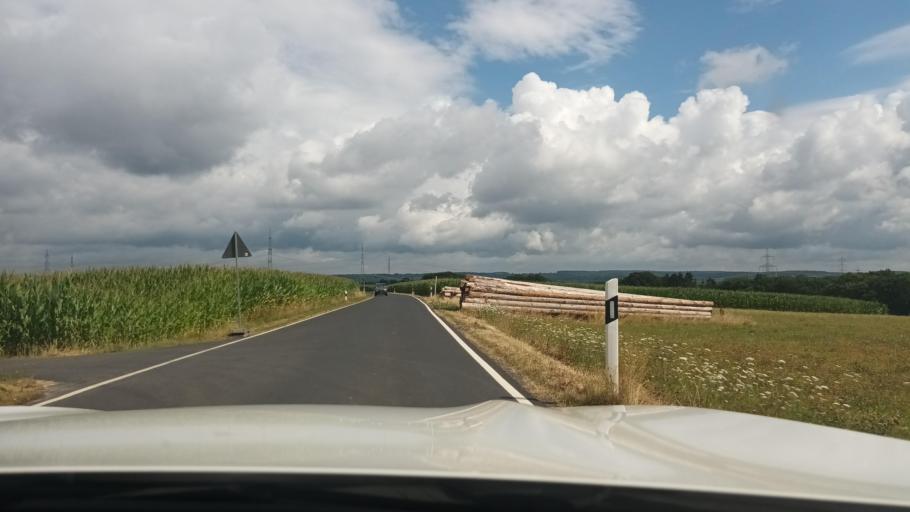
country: DE
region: North Rhine-Westphalia
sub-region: Regierungsbezirk Koln
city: Hennef
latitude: 50.7450
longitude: 7.3516
